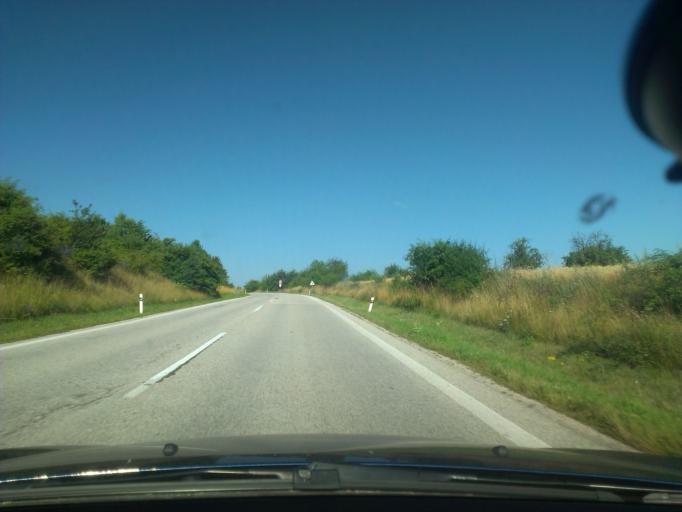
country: SK
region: Trenciansky
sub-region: Okres Myjava
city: Myjava
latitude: 48.7568
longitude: 17.5947
